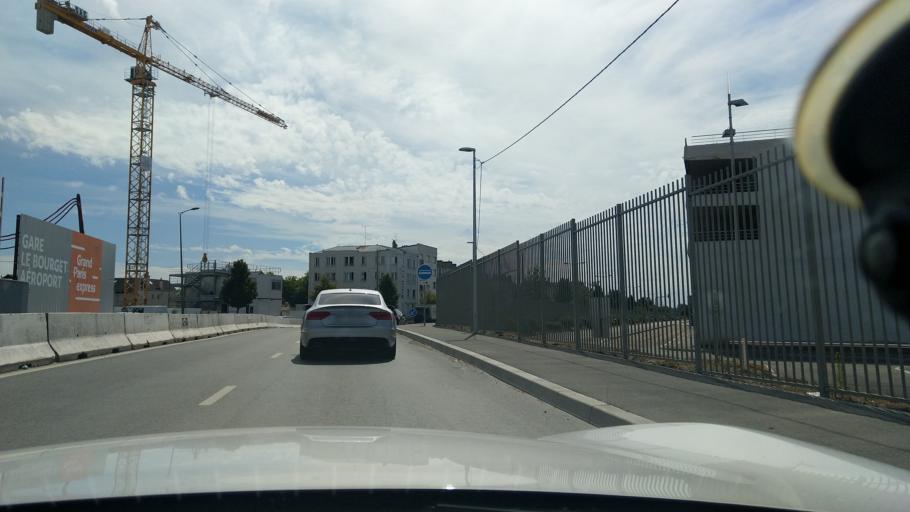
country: FR
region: Ile-de-France
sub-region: Departement de Seine-Saint-Denis
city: Le Bourget
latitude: 48.9467
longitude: 2.4359
